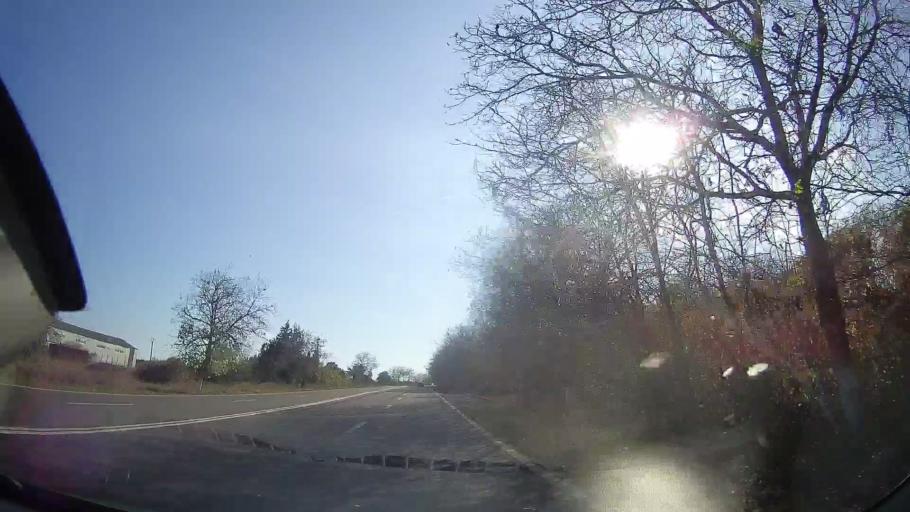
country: RO
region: Constanta
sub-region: Comuna Douazeci si Trei August
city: Dulcesti
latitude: 43.8886
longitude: 28.5728
